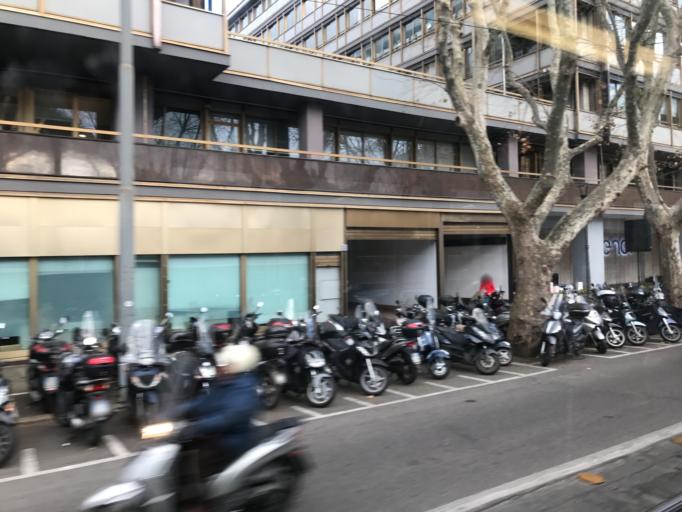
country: IT
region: Latium
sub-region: Citta metropolitana di Roma Capitale
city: Rome
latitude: 41.9165
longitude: 12.5023
